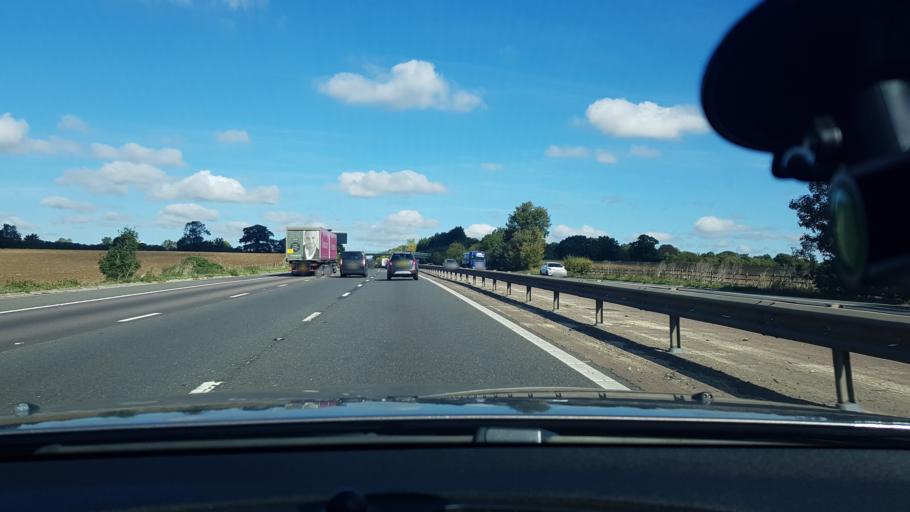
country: GB
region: England
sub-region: Hertfordshire
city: Sawbridgeworth
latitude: 51.7969
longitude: 0.1746
